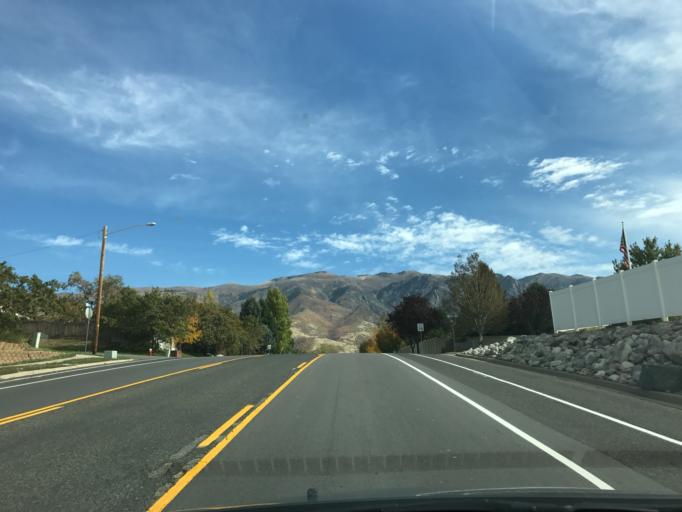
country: US
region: Utah
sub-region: Davis County
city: South Weber
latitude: 41.0889
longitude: -111.9345
